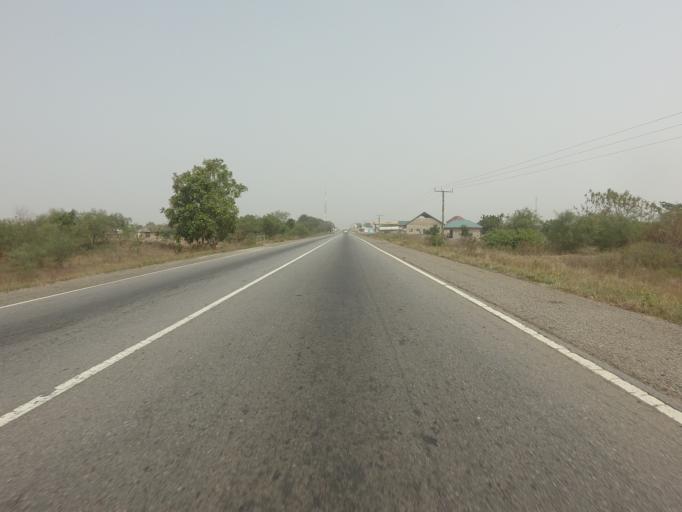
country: GH
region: Volta
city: Anloga
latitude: 5.8826
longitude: 0.4202
